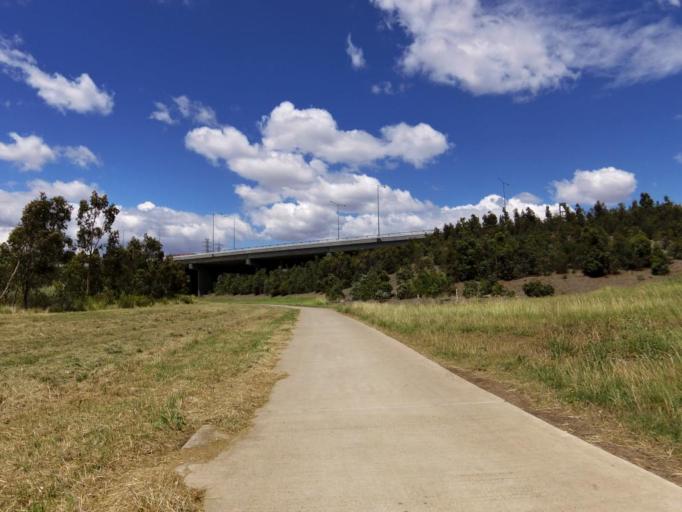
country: AU
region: Victoria
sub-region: Hume
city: Jacana
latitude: -37.6924
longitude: 144.9050
